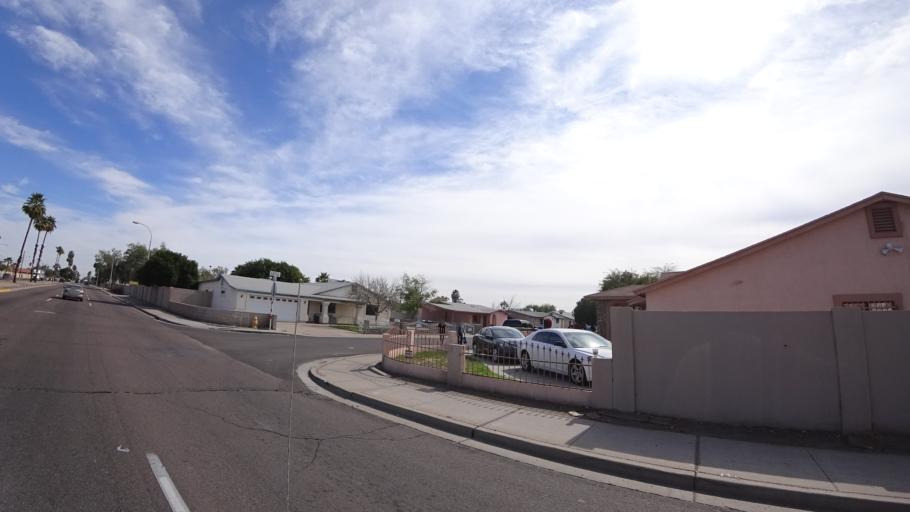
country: US
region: Arizona
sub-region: Maricopa County
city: Tolleson
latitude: 33.4802
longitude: -112.2161
